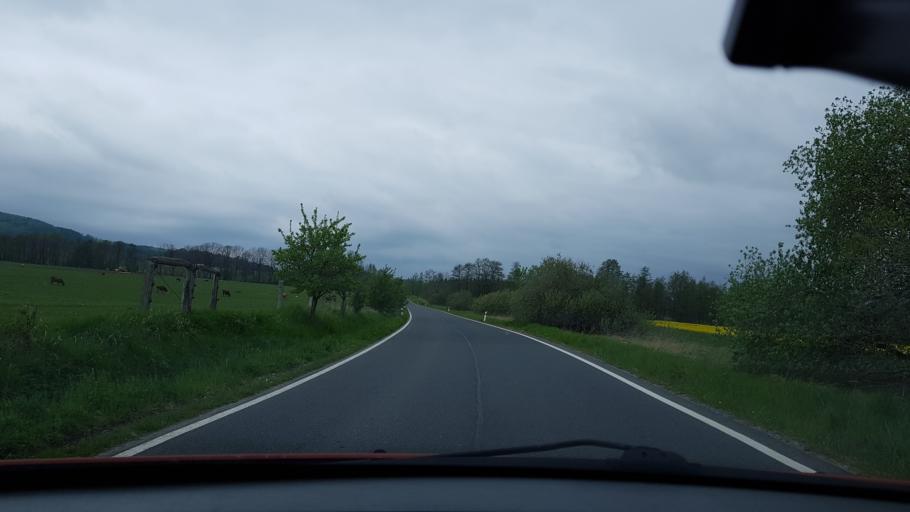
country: PL
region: Opole Voivodeship
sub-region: Powiat nyski
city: Kamienica
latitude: 50.4262
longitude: 16.9630
